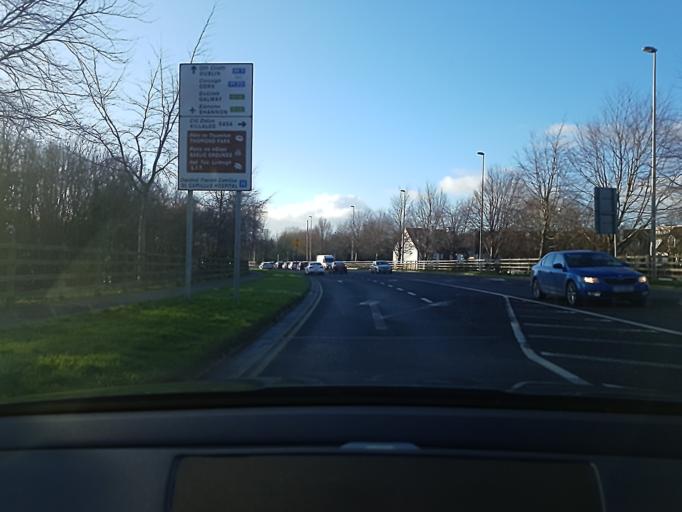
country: IE
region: Munster
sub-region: County Limerick
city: Luimneach
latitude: 52.6633
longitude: -8.6376
